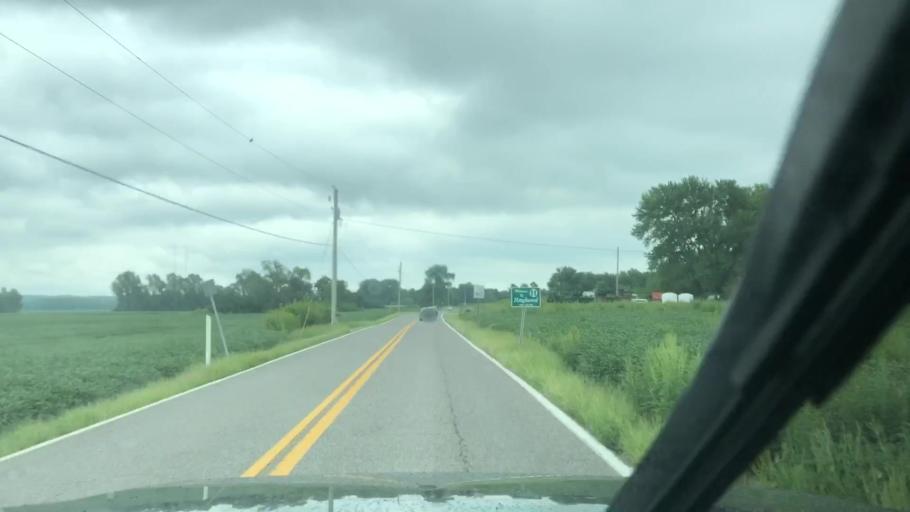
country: US
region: Missouri
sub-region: Saint Louis County
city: Bridgeton
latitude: 38.7971
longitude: -90.4279
